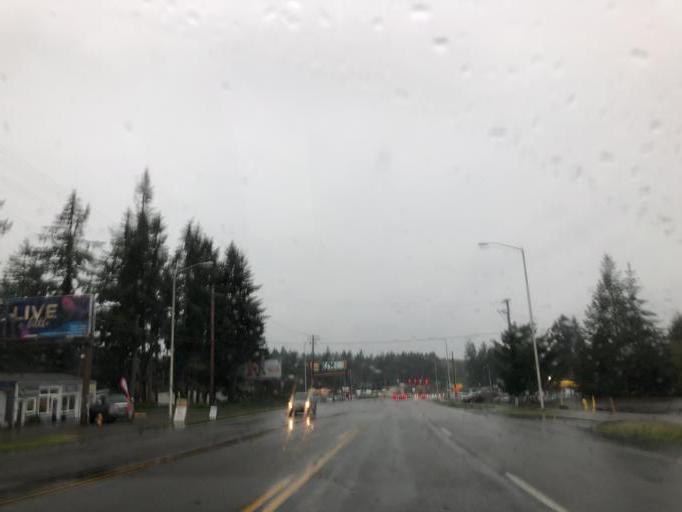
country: US
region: Washington
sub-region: Thurston County
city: Tanglewilde-Thompson Place
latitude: 47.0511
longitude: -122.7932
